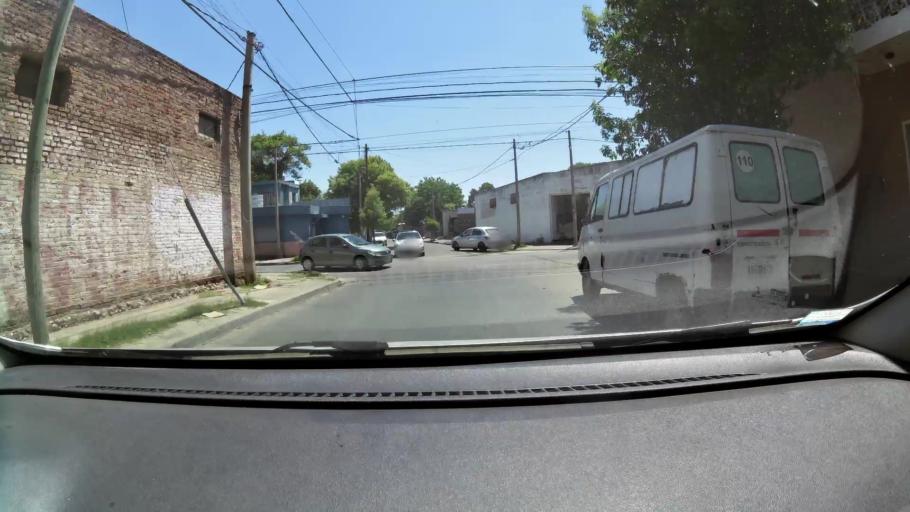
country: AR
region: Cordoba
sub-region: Departamento de Capital
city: Cordoba
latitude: -31.3905
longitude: -64.1464
